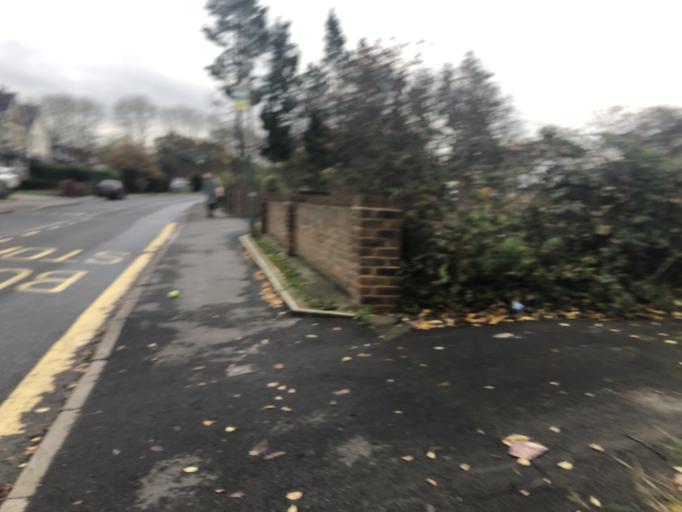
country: GB
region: England
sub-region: Surrey
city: Salfords
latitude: 51.2041
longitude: -0.1647
